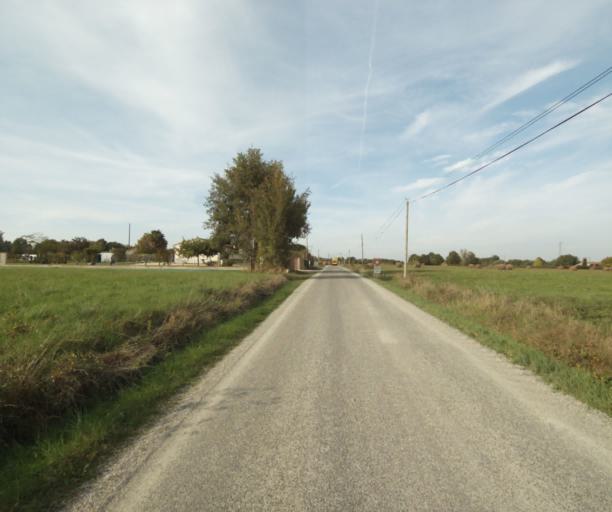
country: FR
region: Midi-Pyrenees
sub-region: Departement du Tarn-et-Garonne
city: Campsas
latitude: 43.9101
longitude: 1.3312
